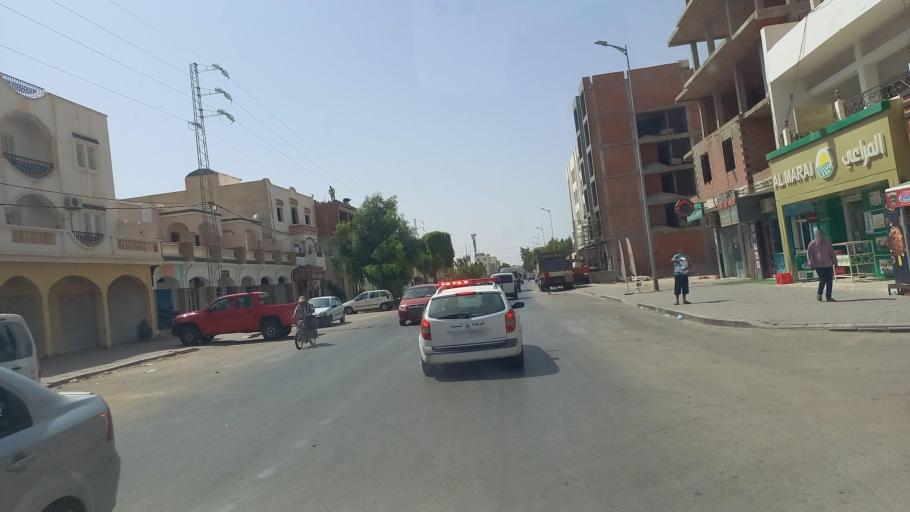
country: TN
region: Madanin
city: Medenine
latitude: 33.3318
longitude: 10.4854
